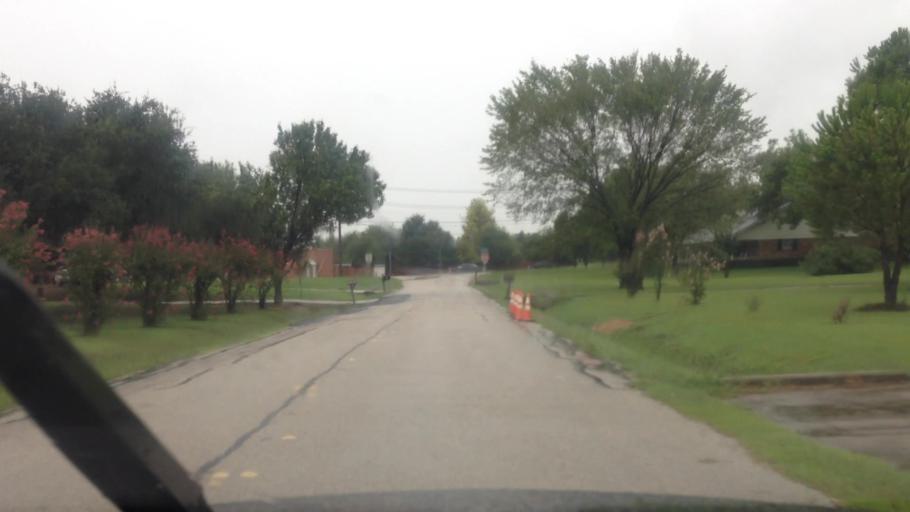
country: US
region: Texas
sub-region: Tarrant County
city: Watauga
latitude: 32.8738
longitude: -97.2254
